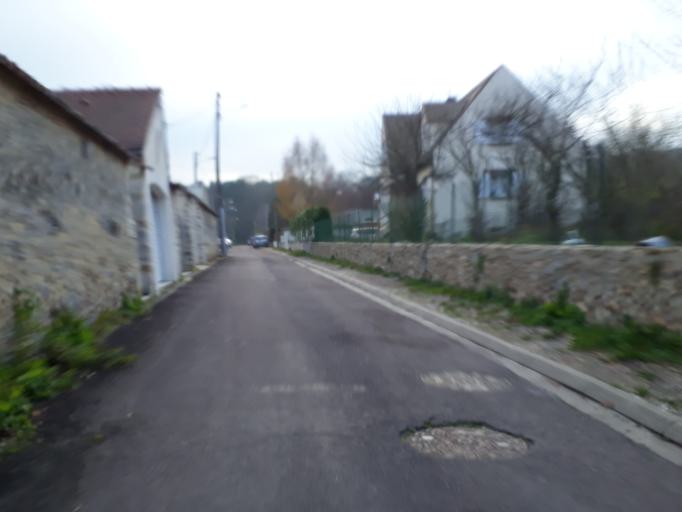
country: FR
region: Ile-de-France
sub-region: Departement de Seine-et-Marne
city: Chartrettes
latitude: 48.4809
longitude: 2.6774
